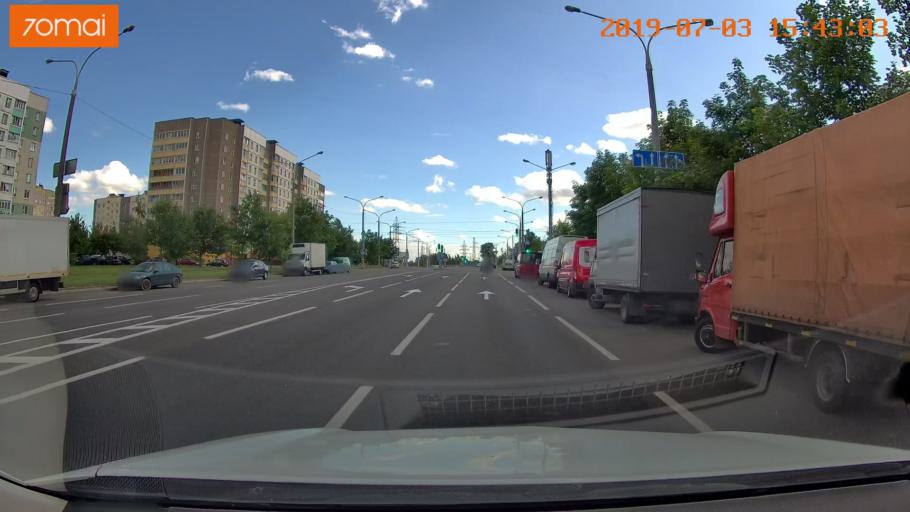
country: BY
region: Minsk
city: Syenitsa
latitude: 53.8377
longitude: 27.5744
